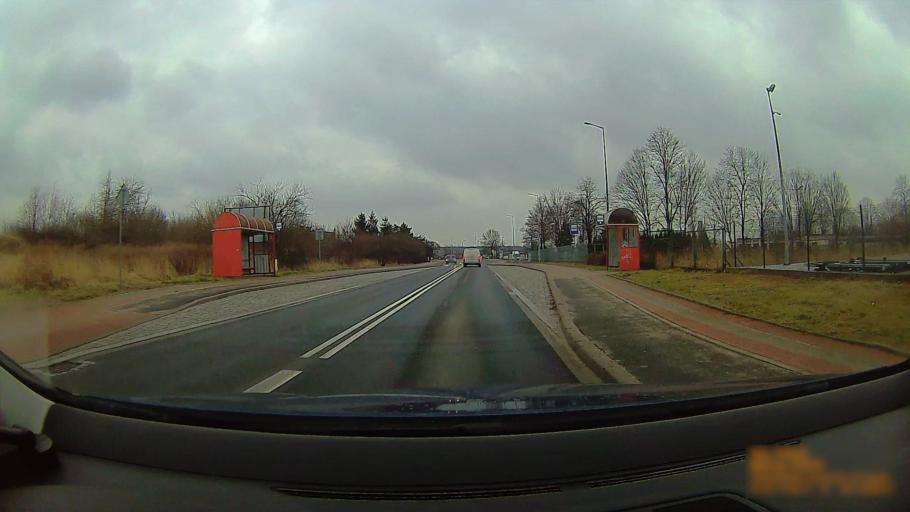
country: PL
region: Greater Poland Voivodeship
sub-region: Konin
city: Konin
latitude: 52.1983
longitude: 18.2610
